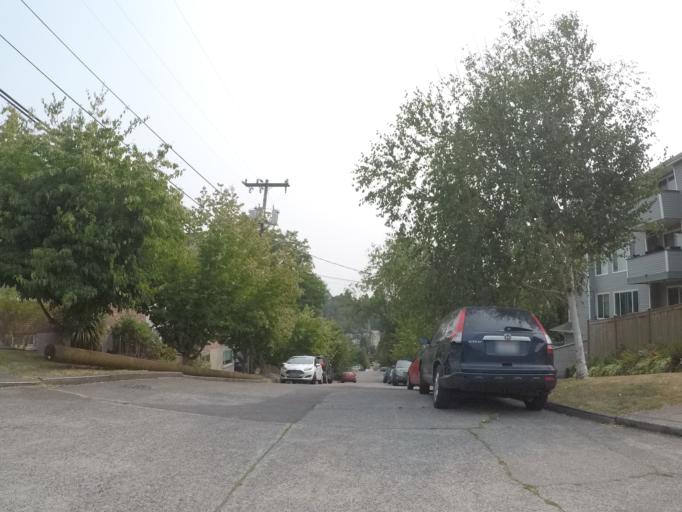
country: US
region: Washington
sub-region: King County
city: Seattle
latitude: 47.6189
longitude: -122.2999
